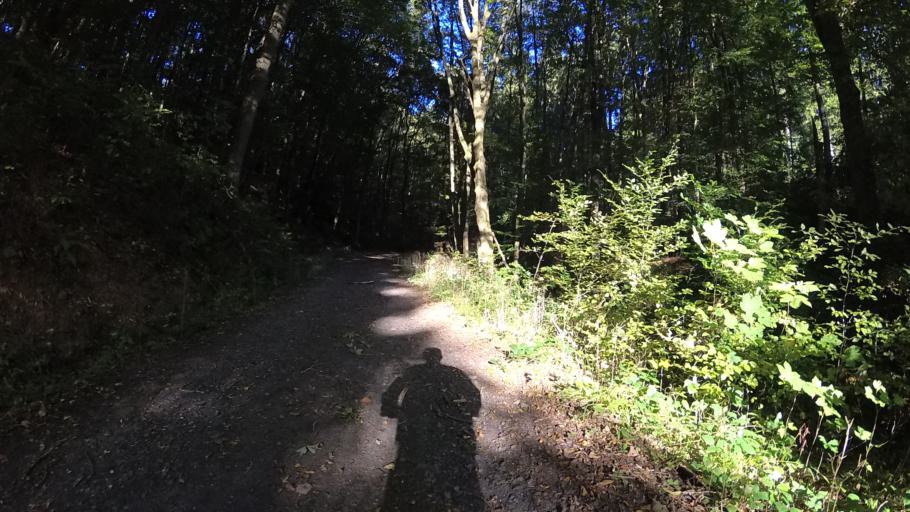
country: DE
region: Saarland
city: Sankt Wendel
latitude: 49.4334
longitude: 7.1812
